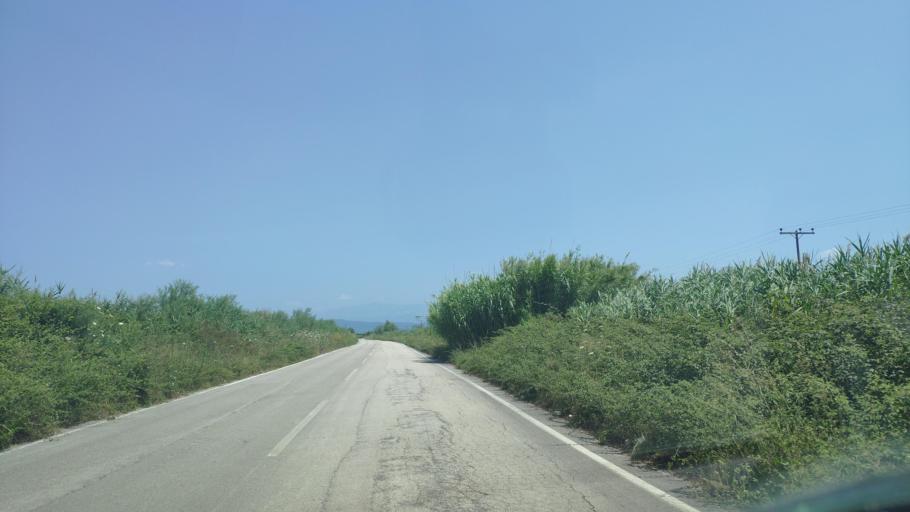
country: GR
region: Epirus
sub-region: Nomos Artas
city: Aneza
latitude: 39.0703
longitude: 20.8793
